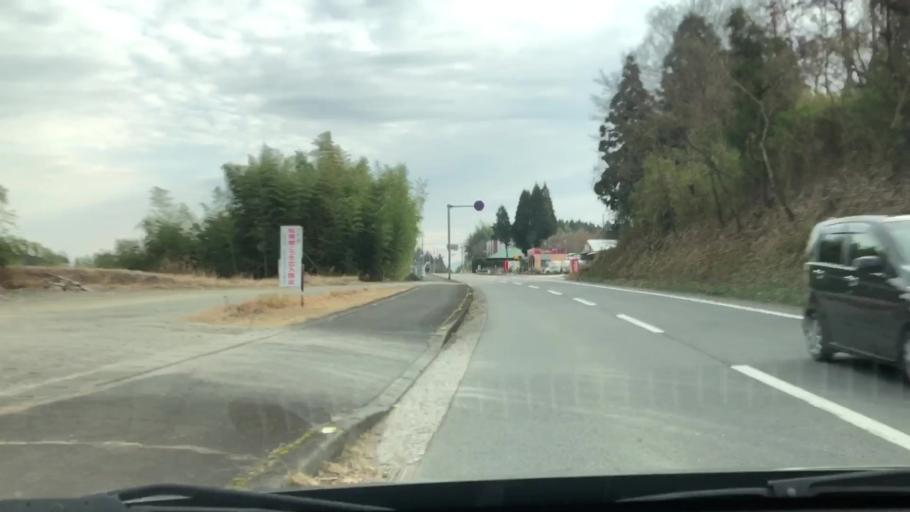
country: JP
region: Oita
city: Takedamachi
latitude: 32.9700
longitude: 131.5694
